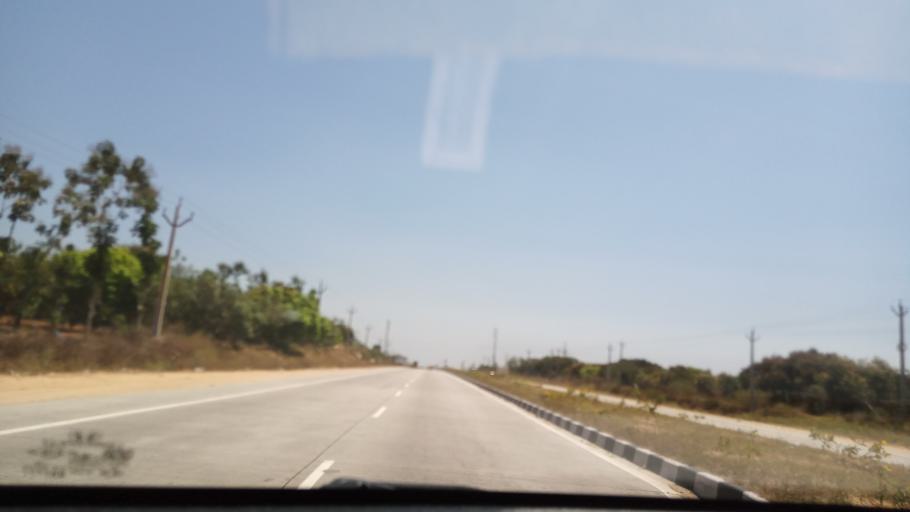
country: IN
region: Andhra Pradesh
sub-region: Chittoor
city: Chittoor
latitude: 13.2011
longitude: 78.9577
